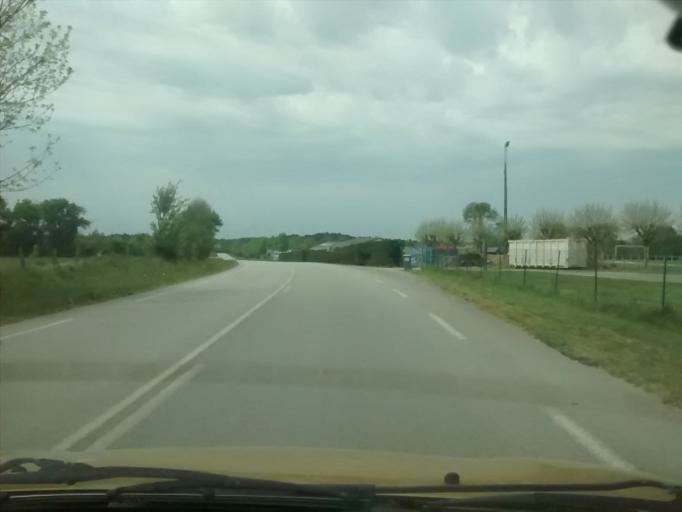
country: FR
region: Brittany
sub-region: Departement du Morbihan
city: Berric
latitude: 47.6292
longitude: -2.5305
